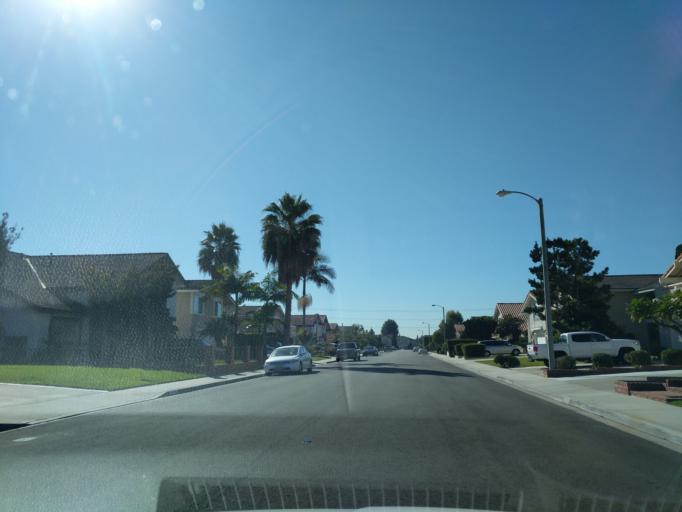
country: US
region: California
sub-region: Orange County
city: Irvine
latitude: 33.7036
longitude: -117.7938
